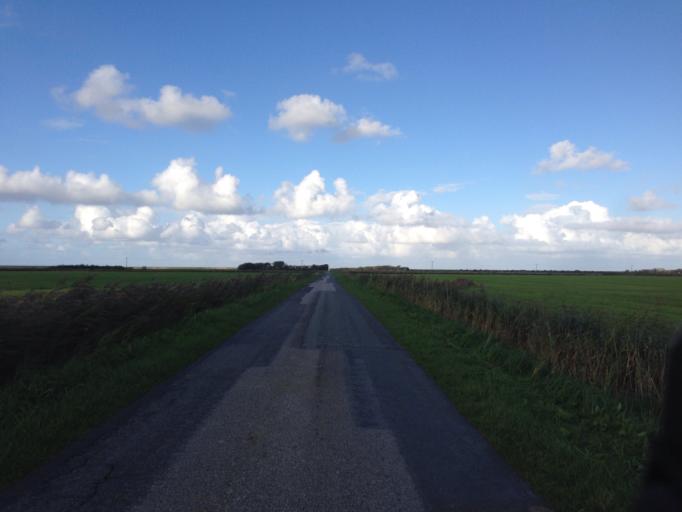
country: DE
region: Schleswig-Holstein
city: Oldsum
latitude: 54.7318
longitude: 8.4781
